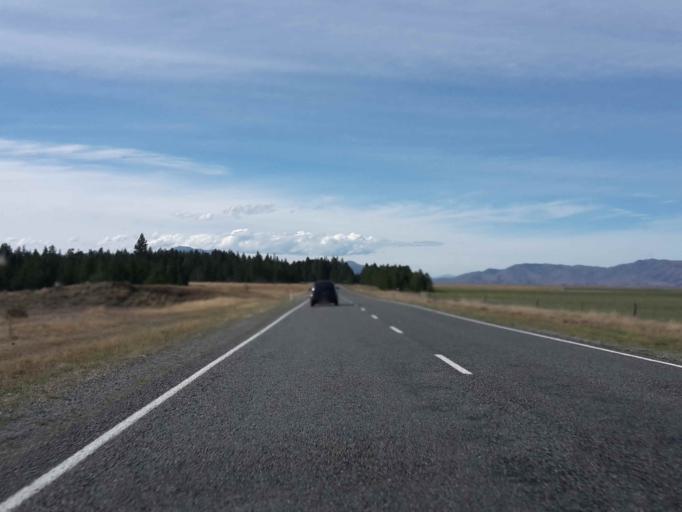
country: NZ
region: Canterbury
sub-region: Timaru District
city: Pleasant Point
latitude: -44.1836
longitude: 170.3108
